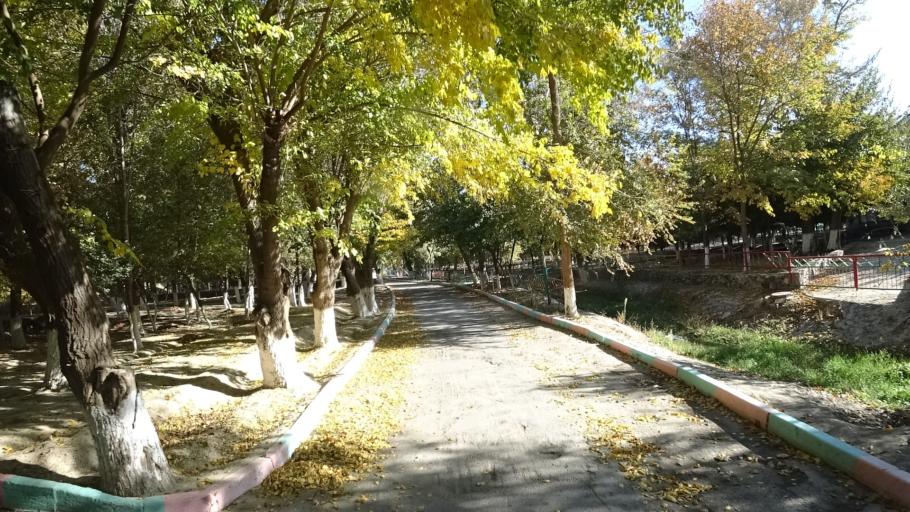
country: UZ
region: Navoiy
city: Karmana Shahri
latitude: 40.2908
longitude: 65.6001
